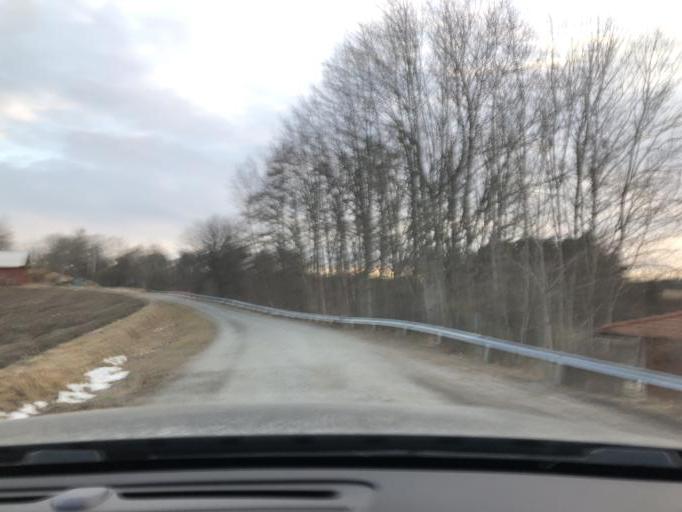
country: SE
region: Uppsala
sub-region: Uppsala Kommun
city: Gamla Uppsala
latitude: 59.9234
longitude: 17.6289
